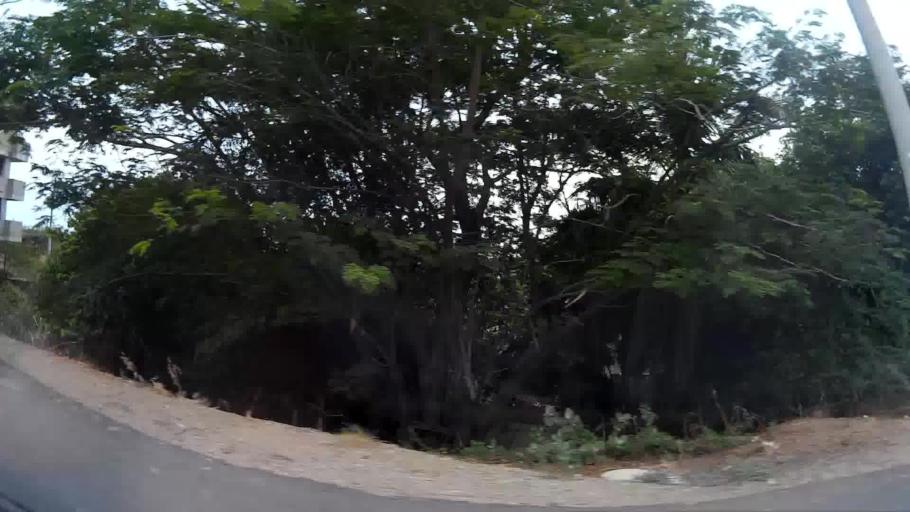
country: CO
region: Magdalena
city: Santa Marta
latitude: 11.1296
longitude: -74.2263
